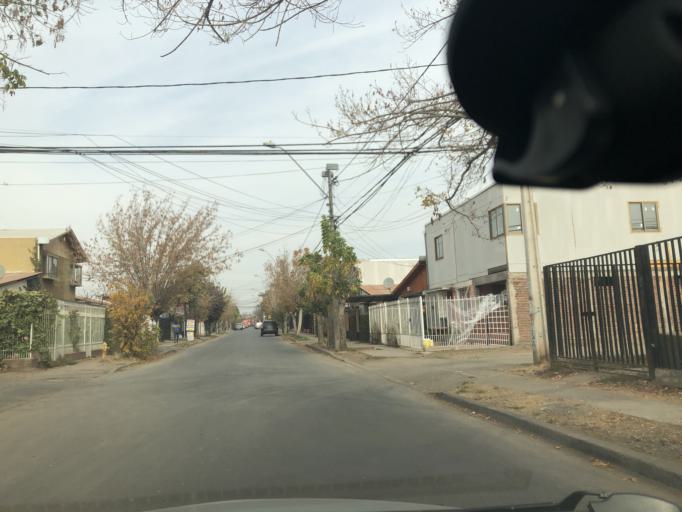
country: CL
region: Santiago Metropolitan
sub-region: Provincia de Cordillera
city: Puente Alto
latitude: -33.5690
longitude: -70.5761
